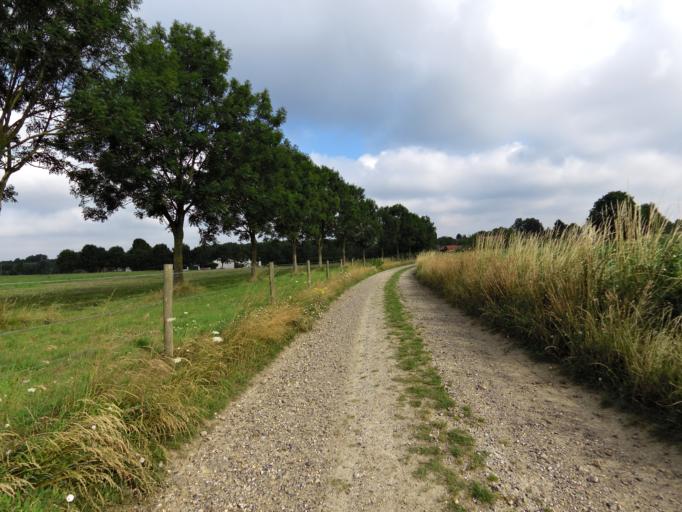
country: NL
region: Limburg
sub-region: Gemeente Nuth
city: Nuth
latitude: 50.8992
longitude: 5.8980
